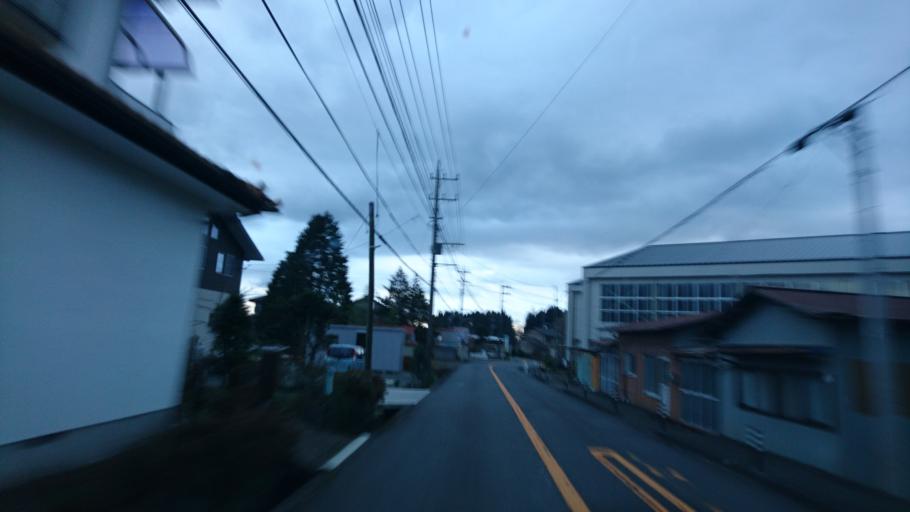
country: JP
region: Shizuoka
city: Fujinomiya
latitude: 35.3146
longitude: 138.5795
